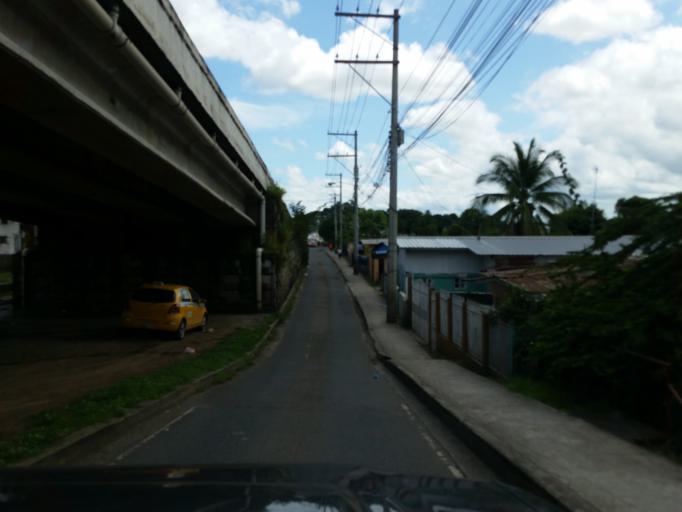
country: PA
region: Panama
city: Tocumen
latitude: 9.0813
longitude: -79.3987
